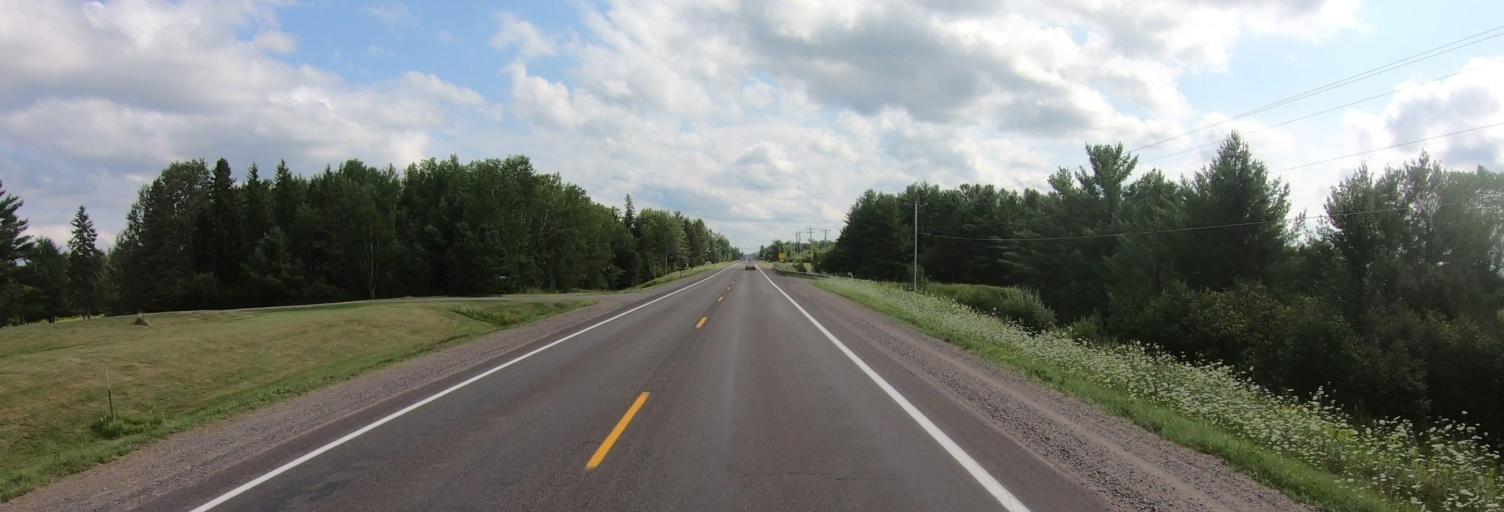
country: US
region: Michigan
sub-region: Ontonagon County
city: Ontonagon
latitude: 46.5478
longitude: -89.1787
